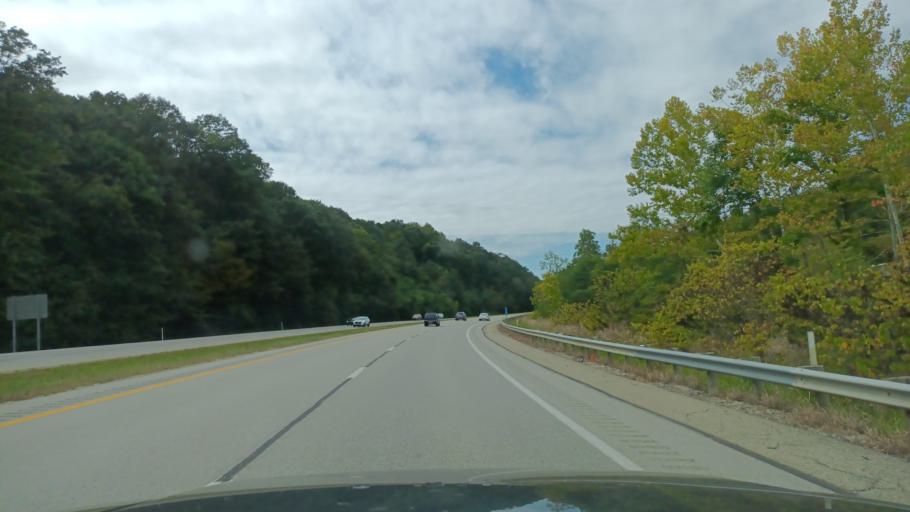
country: US
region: Ohio
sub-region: Washington County
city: Reno
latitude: 39.2443
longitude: -81.3684
